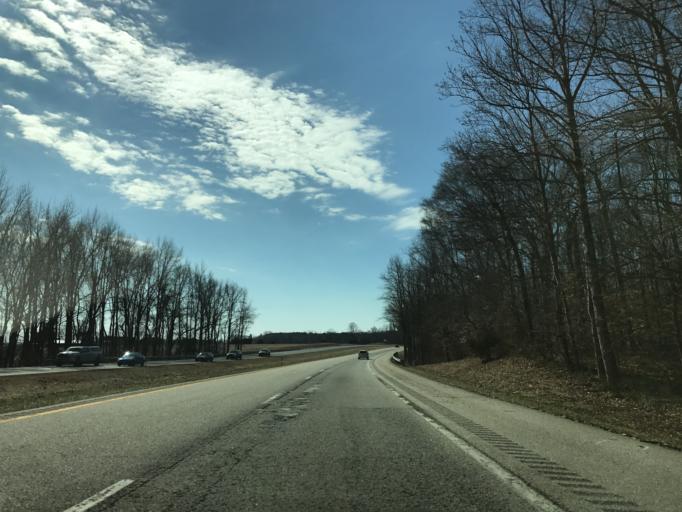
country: US
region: Maryland
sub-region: Queen Anne's County
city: Kingstown
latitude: 39.2062
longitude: -75.8902
